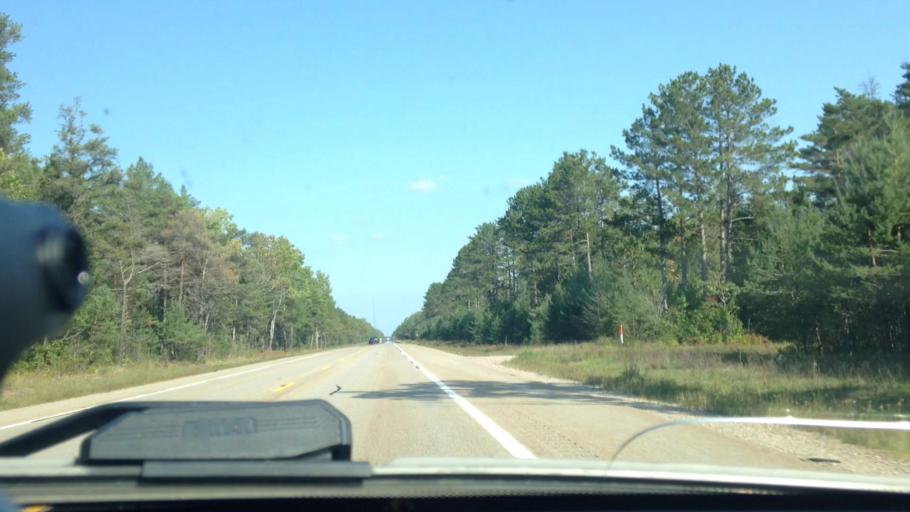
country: US
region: Michigan
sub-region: Chippewa County
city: Sault Ste. Marie
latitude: 46.3662
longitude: -84.7551
